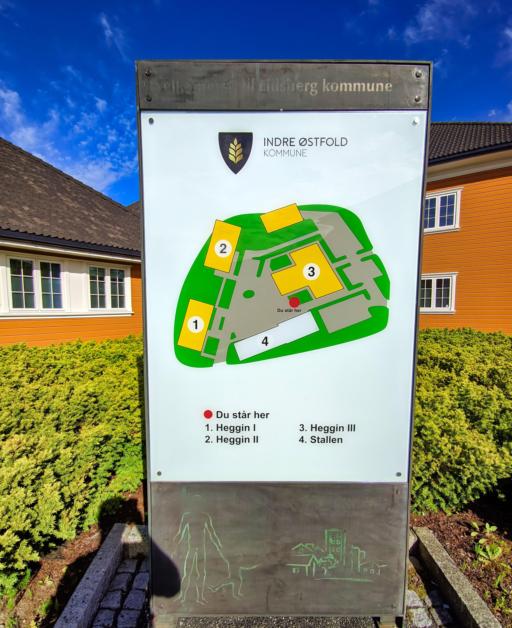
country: NO
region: Ostfold
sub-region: Eidsberg
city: Mysen
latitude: 59.5511
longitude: 11.3364
